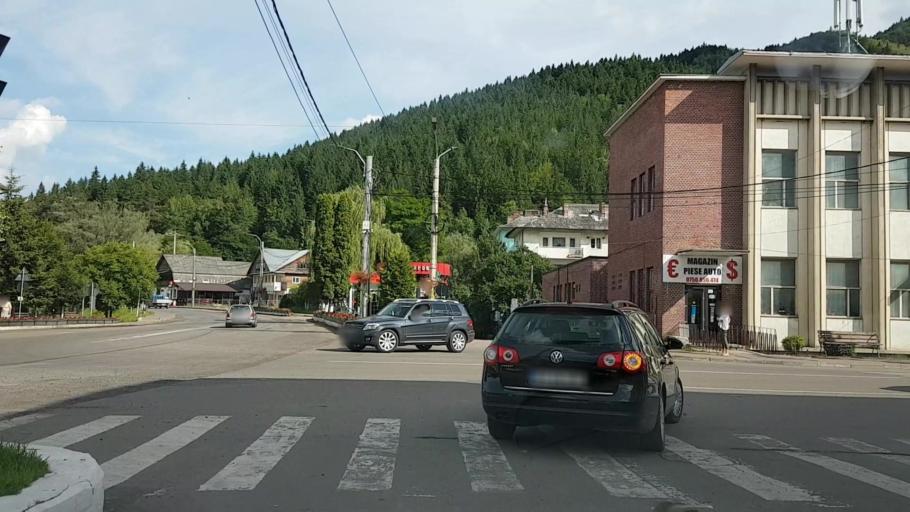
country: RO
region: Neamt
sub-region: Comuna Bicaz
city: Dodeni
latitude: 46.9116
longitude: 26.0882
